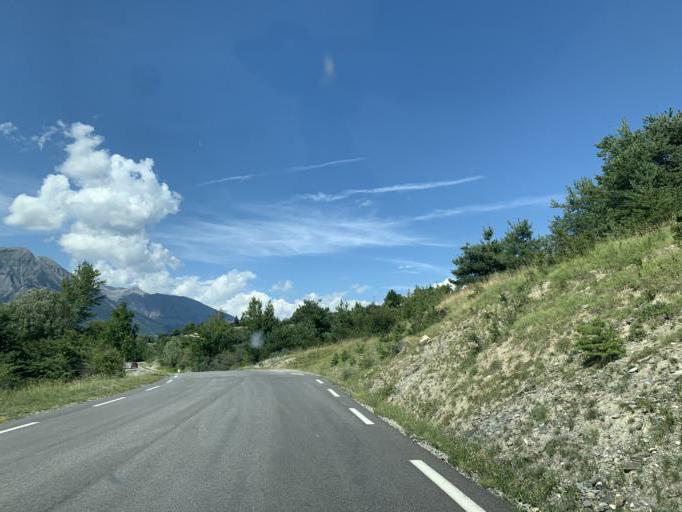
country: FR
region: Provence-Alpes-Cote d'Azur
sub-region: Departement des Hautes-Alpes
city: Embrun
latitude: 44.5697
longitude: 6.5226
